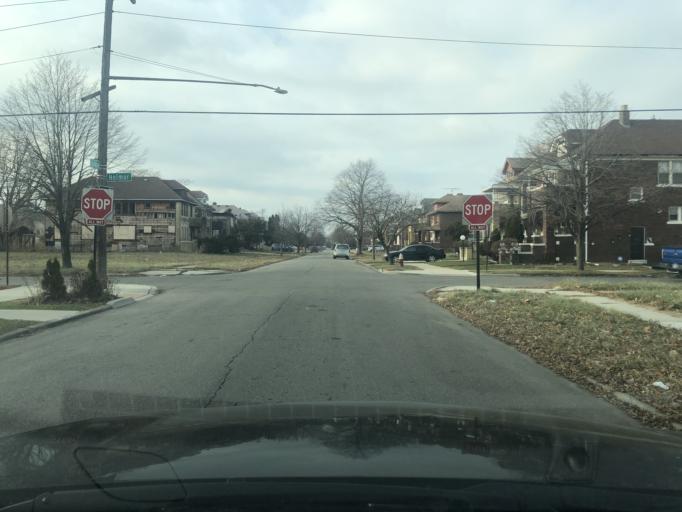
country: US
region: Michigan
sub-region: Wayne County
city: Highland Park
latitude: 42.3905
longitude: -83.1341
